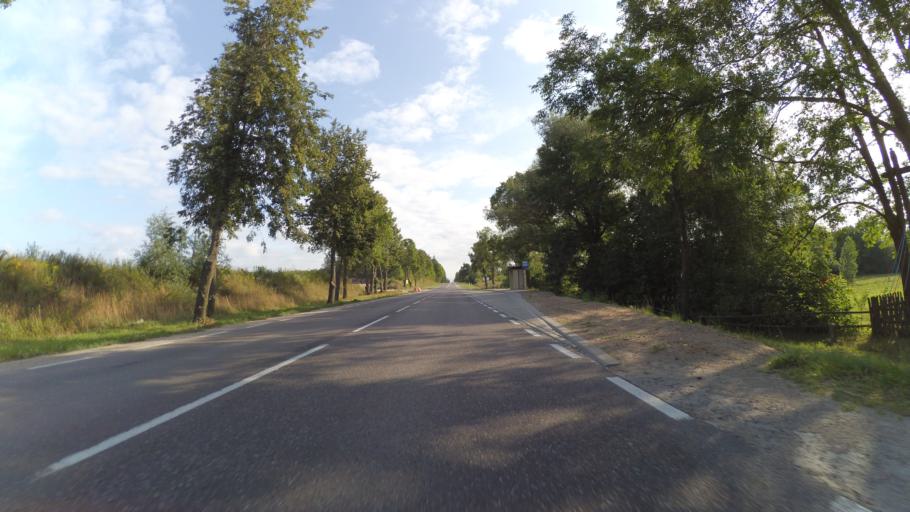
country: PL
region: Podlasie
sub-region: Powiat sokolski
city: Sokolka
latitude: 53.3632
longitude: 23.4214
